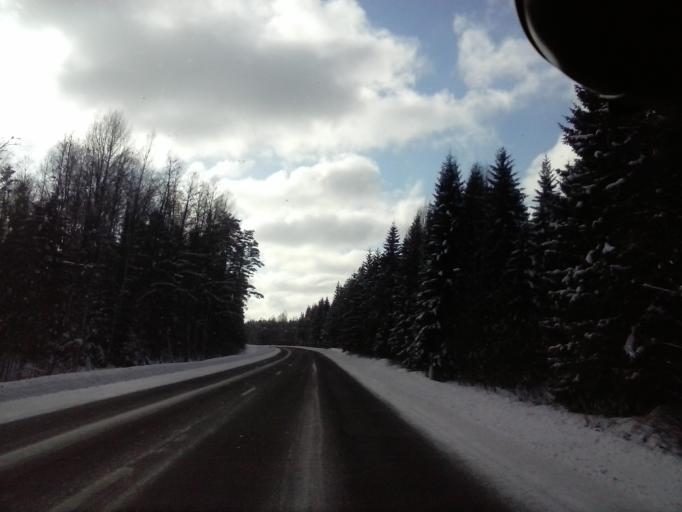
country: EE
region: Viljandimaa
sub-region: Moisakuela linn
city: Moisakula
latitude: 58.2374
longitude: 25.1213
